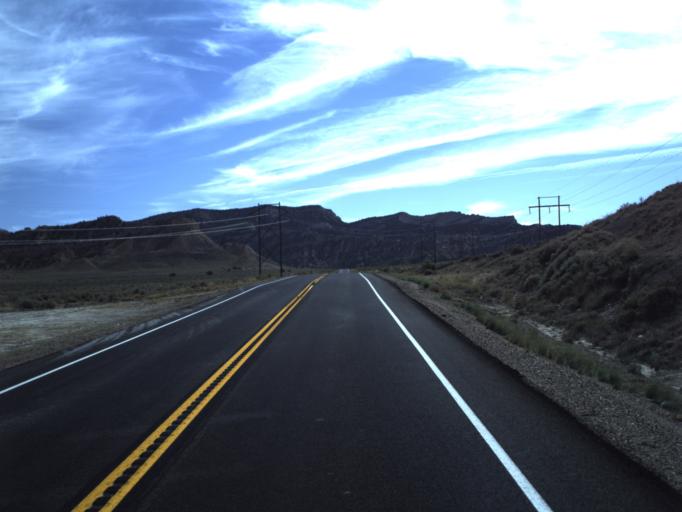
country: US
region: Utah
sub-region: Garfield County
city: Panguitch
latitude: 37.6021
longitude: -111.9605
